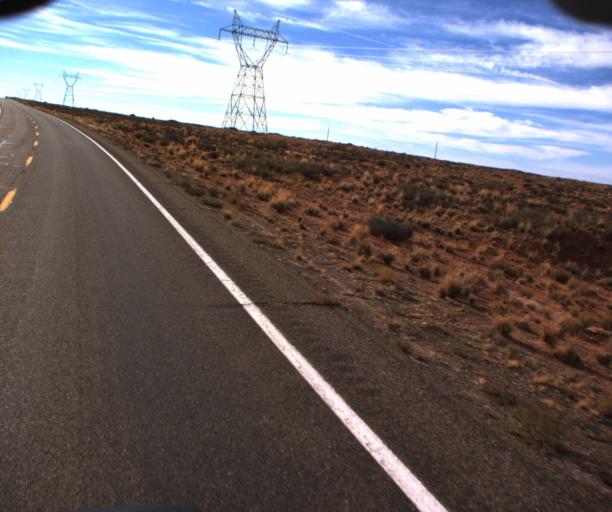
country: US
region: Arizona
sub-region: Coconino County
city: LeChee
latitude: 36.8564
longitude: -111.3369
